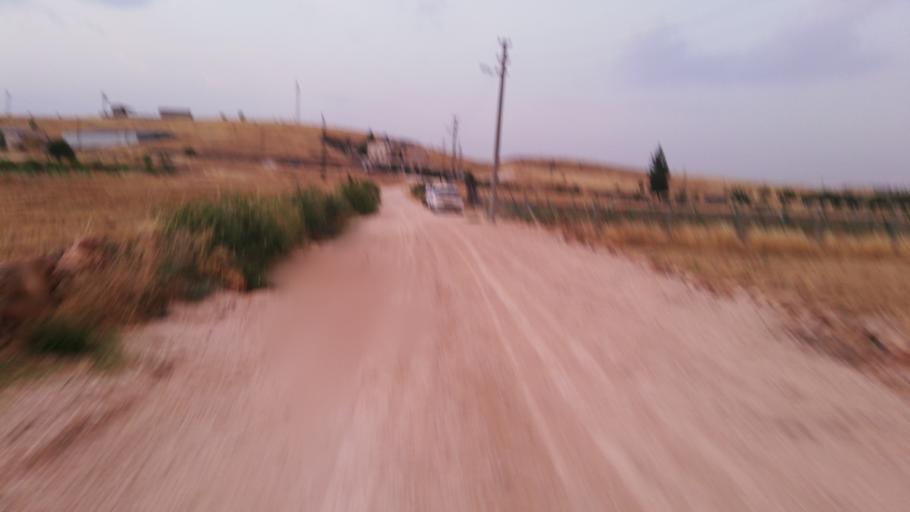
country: TR
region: Mardin
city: Kindirip
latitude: 37.4594
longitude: 41.2212
